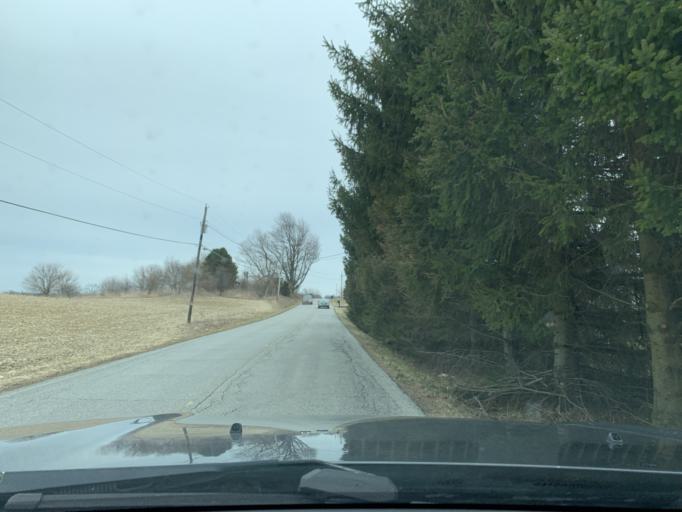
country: US
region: Indiana
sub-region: Porter County
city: Chesterton
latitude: 41.5860
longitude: -87.0174
